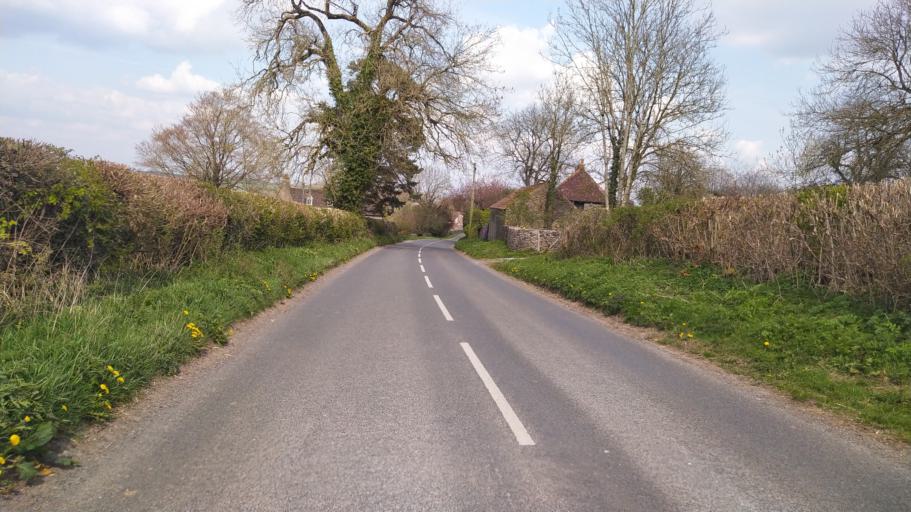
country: GB
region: England
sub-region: Bath and North East Somerset
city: Radstock
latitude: 51.2326
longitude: -2.4043
